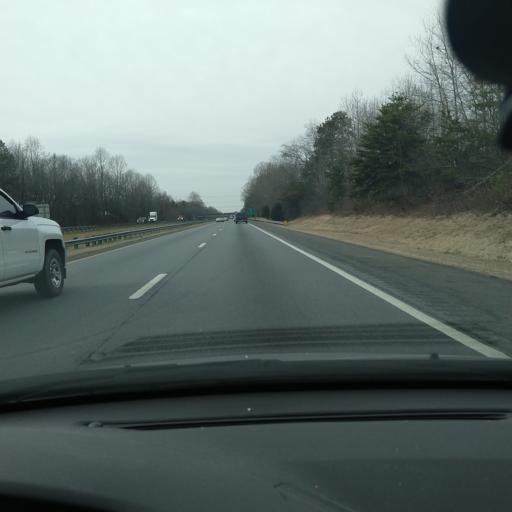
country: US
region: North Carolina
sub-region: Cleveland County
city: White Plains
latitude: 35.1712
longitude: -81.4297
